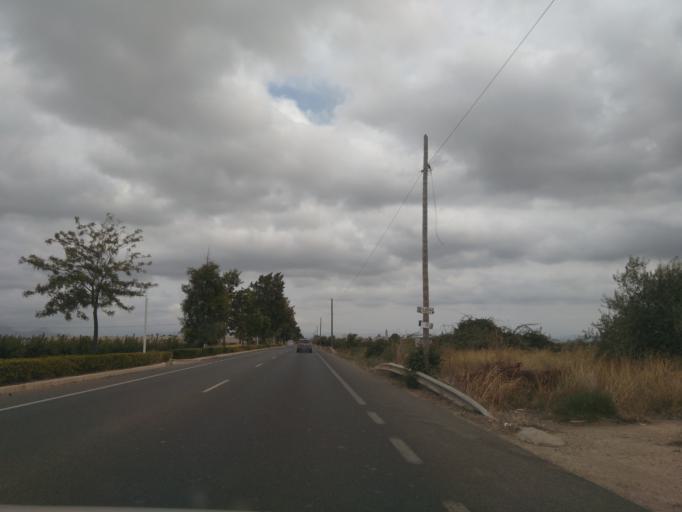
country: ES
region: Valencia
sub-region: Provincia de Valencia
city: Carlet
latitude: 39.2142
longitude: -0.5141
